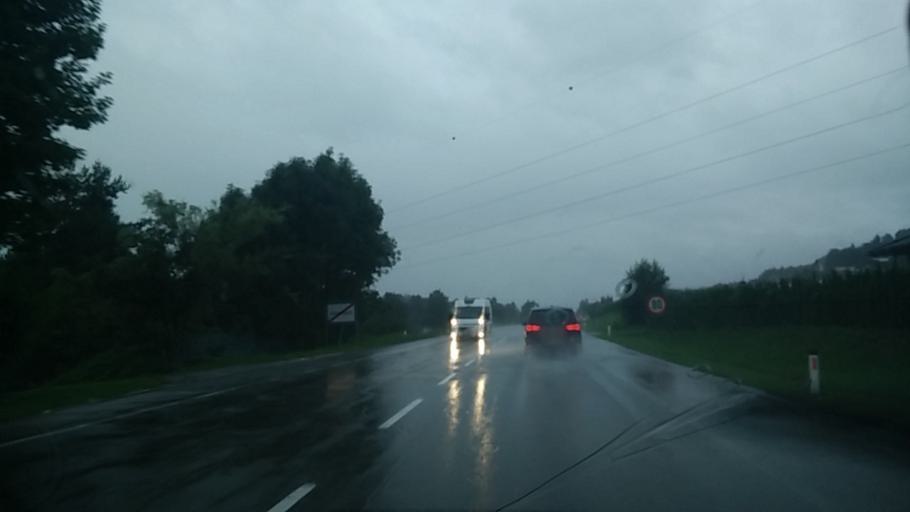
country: AT
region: Carinthia
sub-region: Politischer Bezirk Villach Land
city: Wernberg
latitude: 46.6180
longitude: 13.9547
